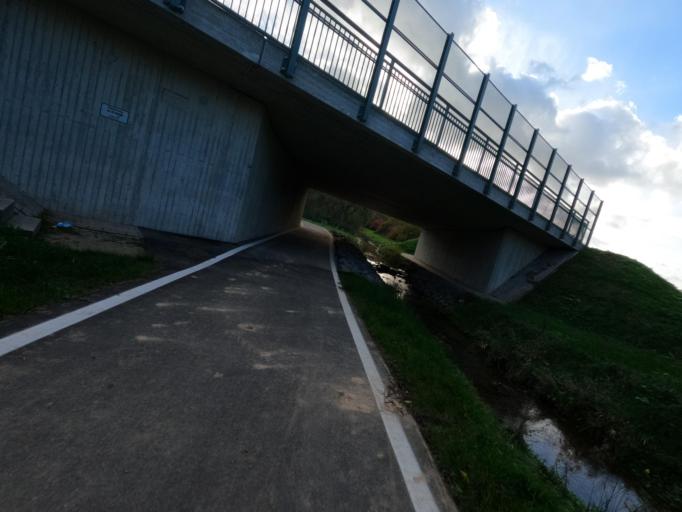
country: DE
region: North Rhine-Westphalia
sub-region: Regierungsbezirk Koln
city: Titz
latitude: 51.0897
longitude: 6.4073
